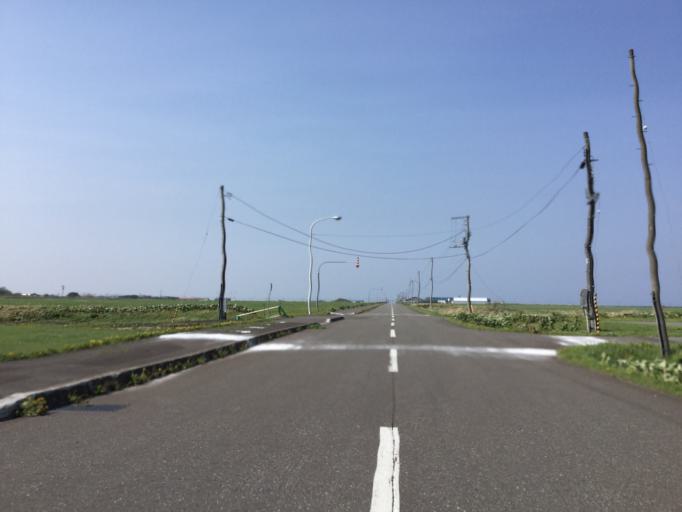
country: JP
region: Hokkaido
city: Makubetsu
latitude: 45.3907
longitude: 141.7674
